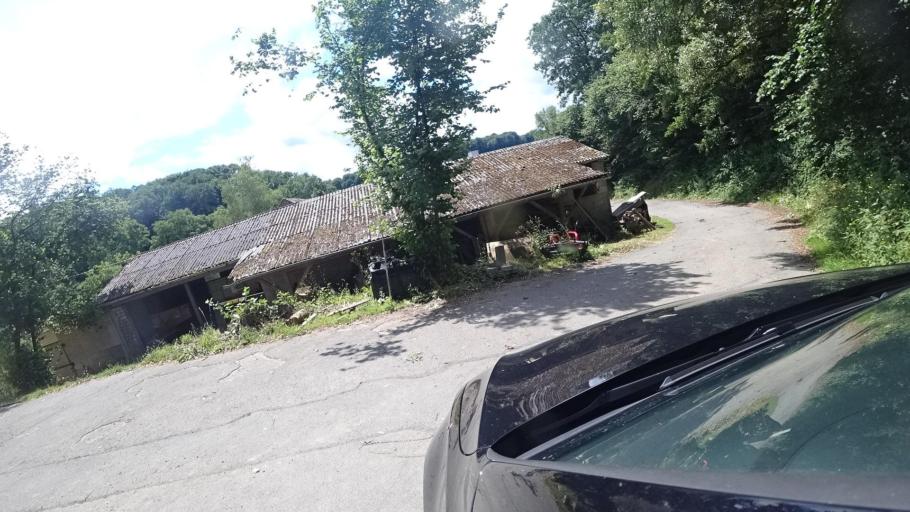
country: DE
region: Rheinland-Pfalz
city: Orfgen
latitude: 50.6555
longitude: 7.5168
